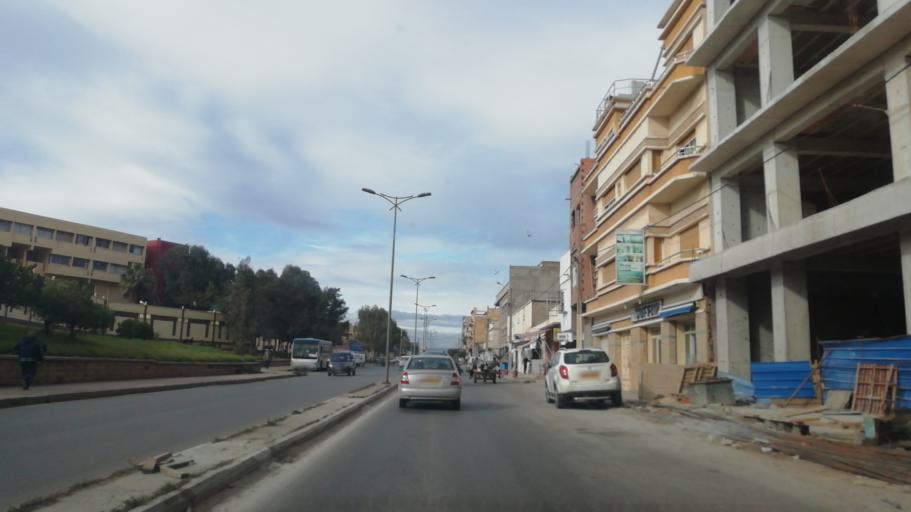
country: DZ
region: Oran
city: Bir el Djir
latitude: 35.7127
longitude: -0.5902
